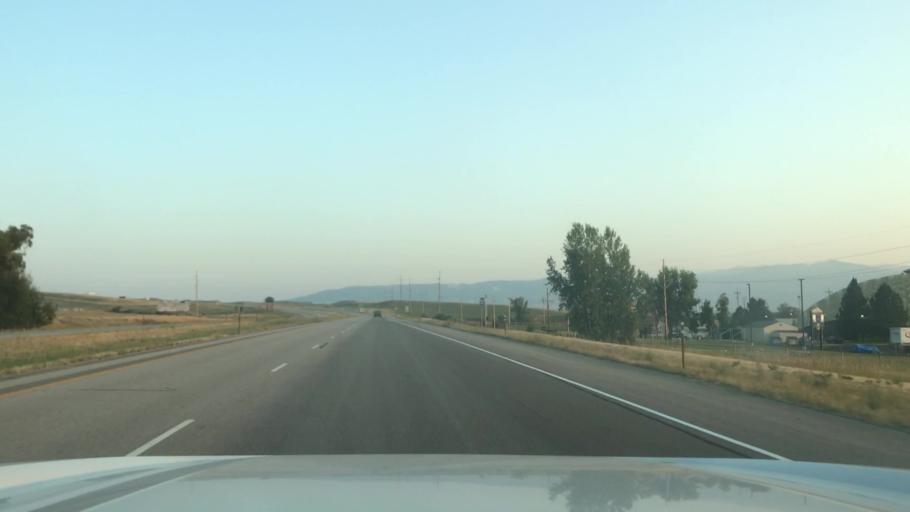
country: US
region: Wyoming
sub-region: Sheridan County
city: Sheridan
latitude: 44.7663
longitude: -106.9370
